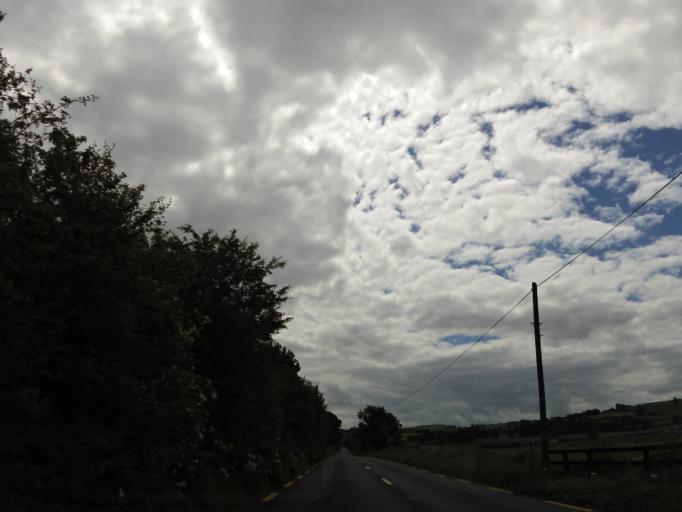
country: IE
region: Munster
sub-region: North Tipperary
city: Nenagh
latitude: 52.7810
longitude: -8.0319
